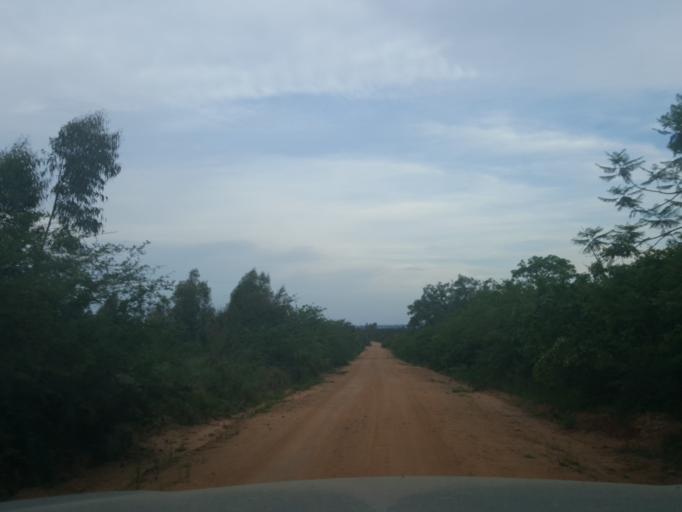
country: ZA
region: Limpopo
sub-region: Mopani District Municipality
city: Hoedspruit
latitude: -24.5880
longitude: 30.9600
